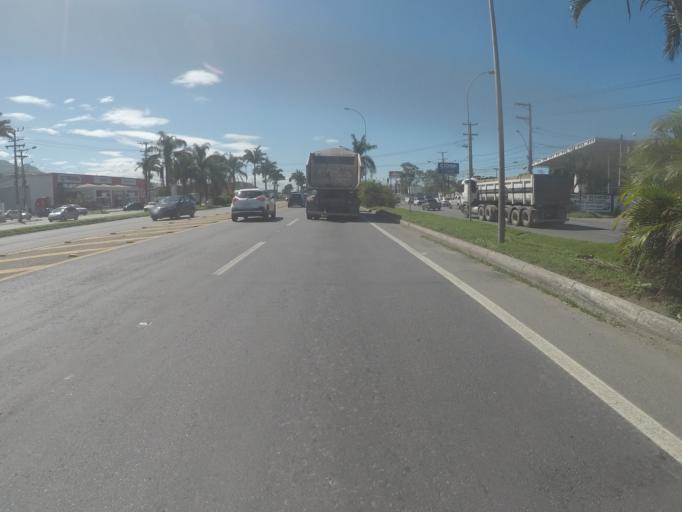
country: BR
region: Espirito Santo
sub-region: Serra
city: Serra
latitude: -20.2069
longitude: -40.2693
